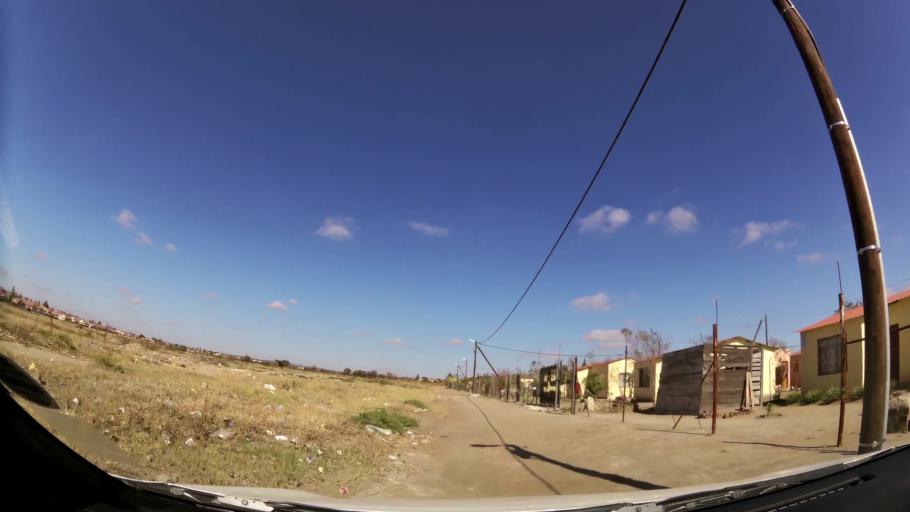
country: ZA
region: Limpopo
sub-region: Capricorn District Municipality
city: Polokwane
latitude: -23.8611
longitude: 29.3979
